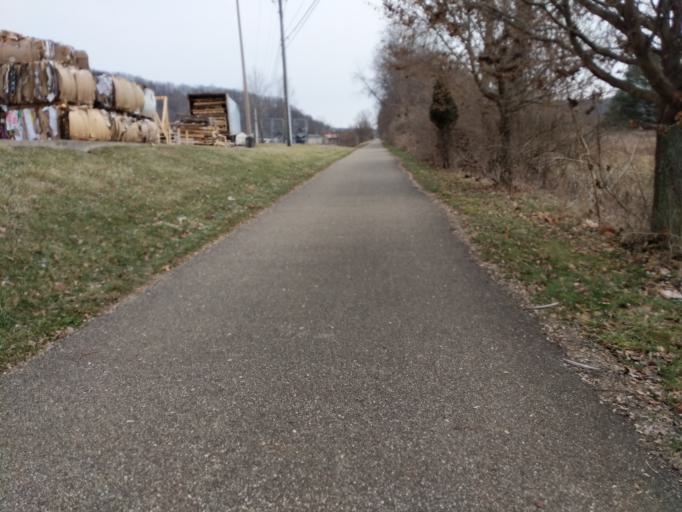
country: US
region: Ohio
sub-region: Athens County
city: Athens
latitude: 39.3344
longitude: -82.0589
